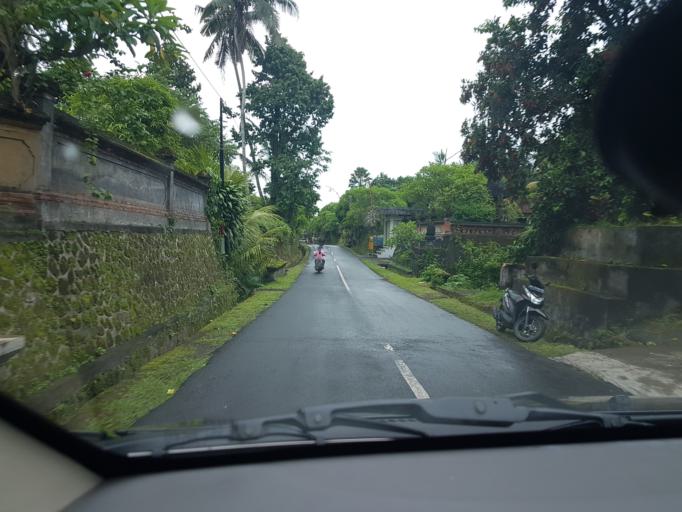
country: ID
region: Bali
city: Banjar Tebongkang
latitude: -8.5310
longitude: 115.2372
